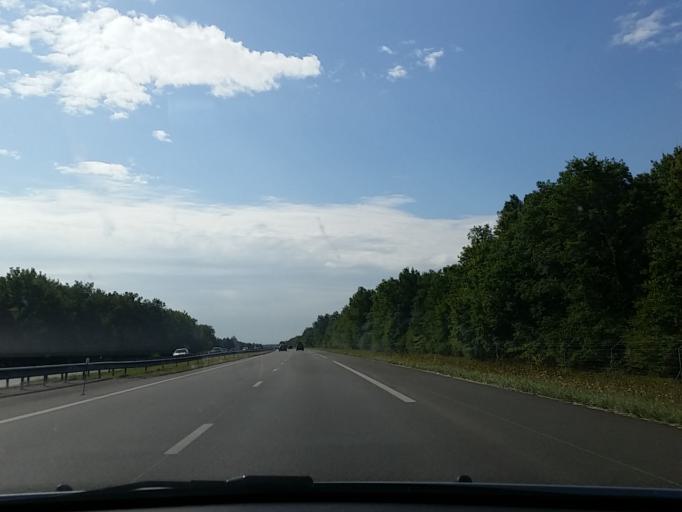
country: FR
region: Centre
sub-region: Departement du Cher
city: Levet
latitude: 46.8819
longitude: 2.4205
